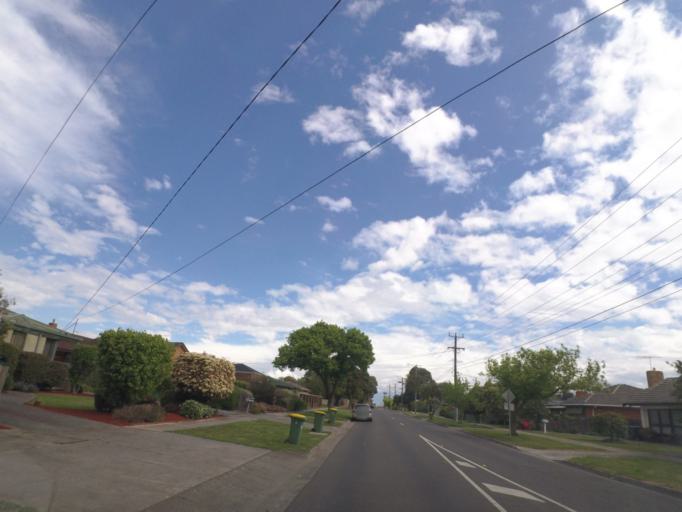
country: AU
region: Victoria
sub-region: Knox
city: Boronia
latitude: -37.8756
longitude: 145.2703
